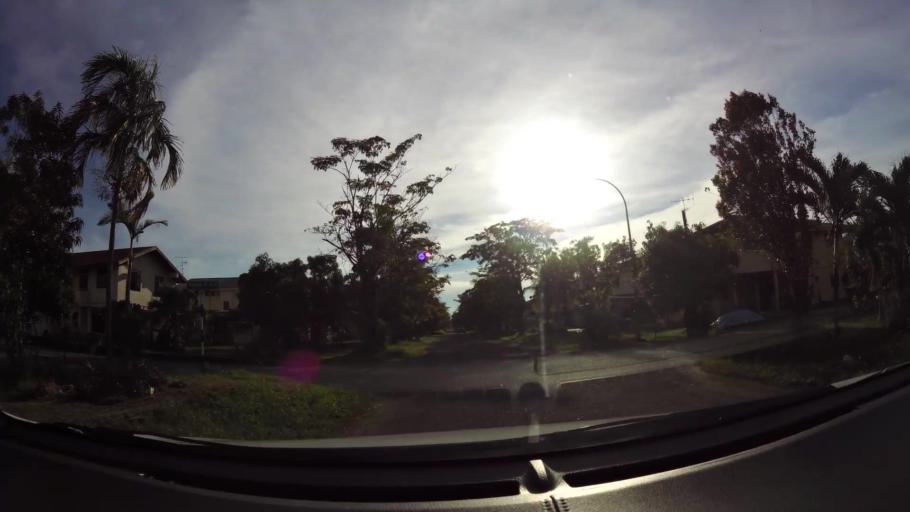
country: BN
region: Belait
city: Kuala Belait
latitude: 4.5770
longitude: 114.2266
